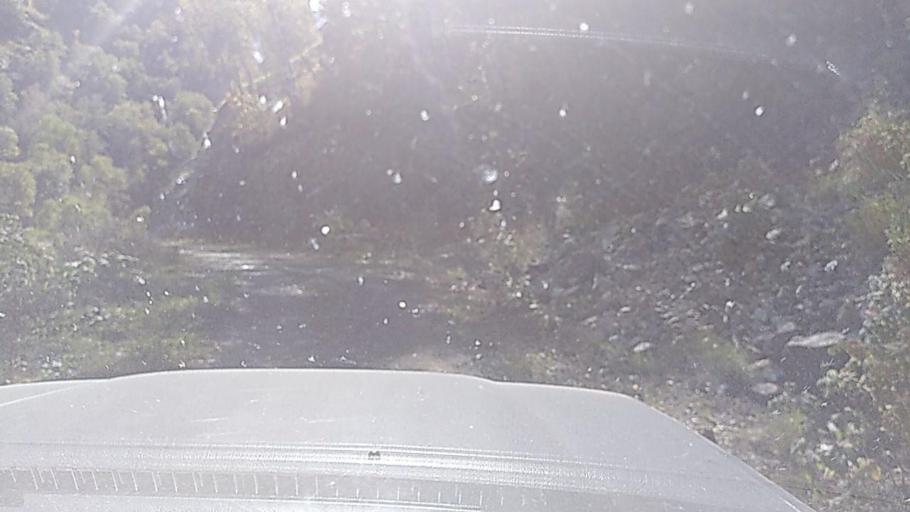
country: RU
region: Kabardino-Balkariya
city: Kamennomostskoye
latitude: 43.7153
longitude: 42.8455
